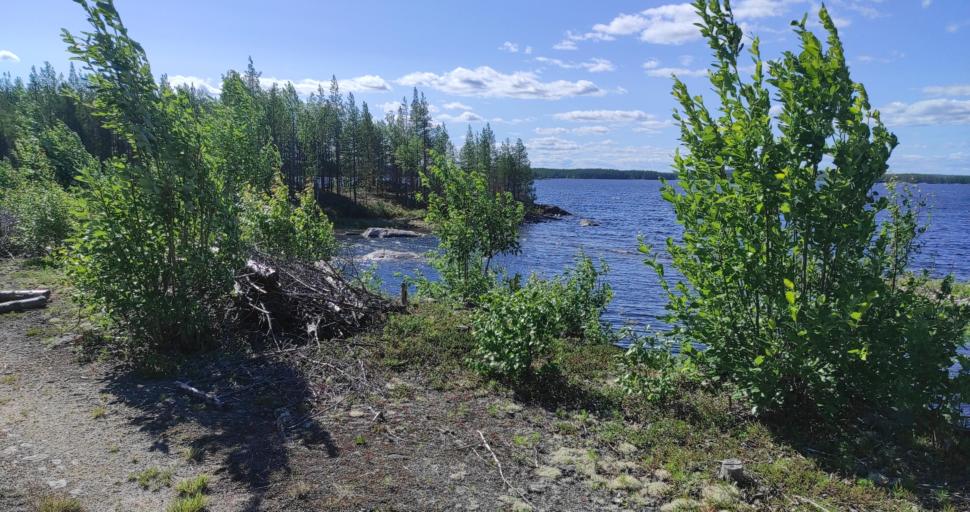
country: RU
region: Murmansk
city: Zelenoborskiy
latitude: 66.6855
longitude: 32.4532
